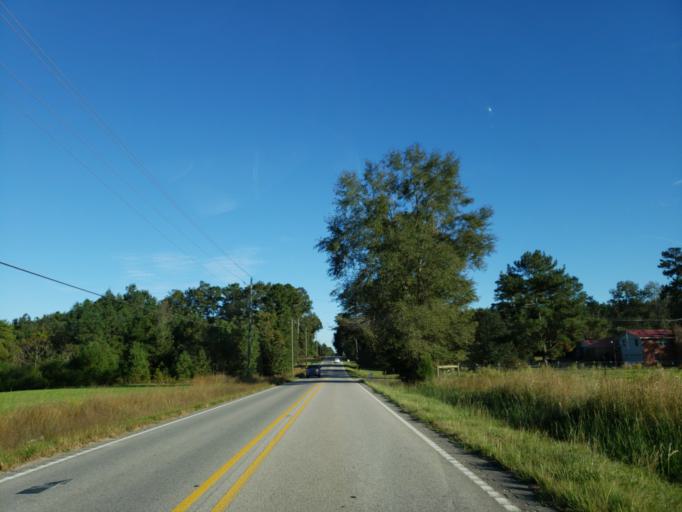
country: US
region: Mississippi
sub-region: Perry County
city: Richton
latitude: 31.3563
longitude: -88.9580
